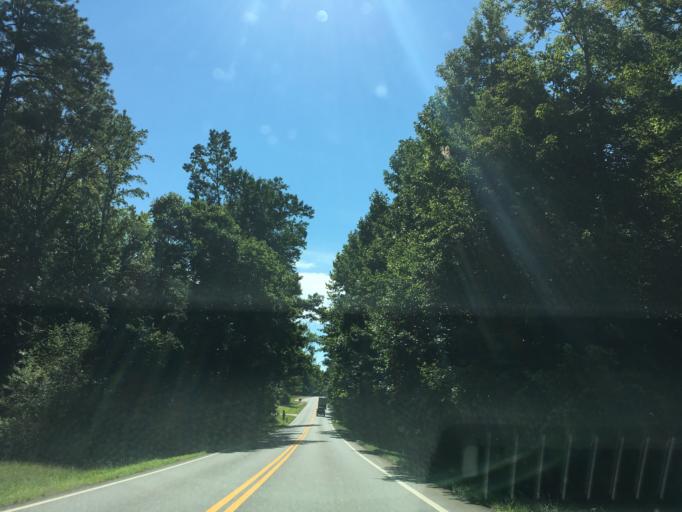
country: US
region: Georgia
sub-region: Fulton County
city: Milton
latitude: 34.1640
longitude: -84.3162
